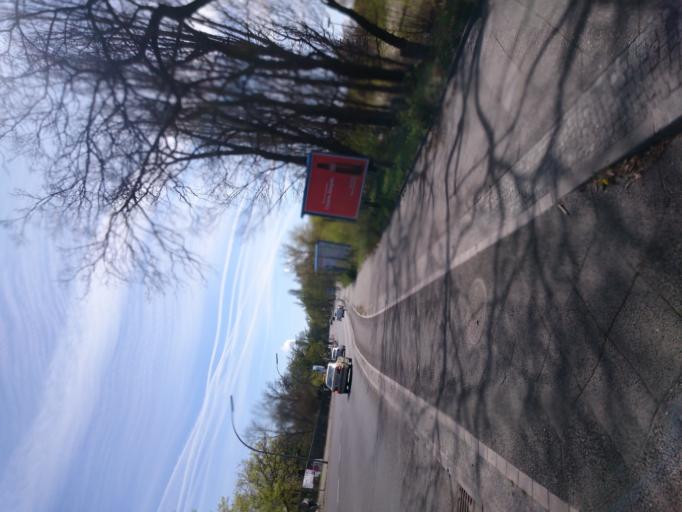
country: DE
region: Berlin
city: Haselhorst
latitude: 52.5504
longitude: 13.2485
